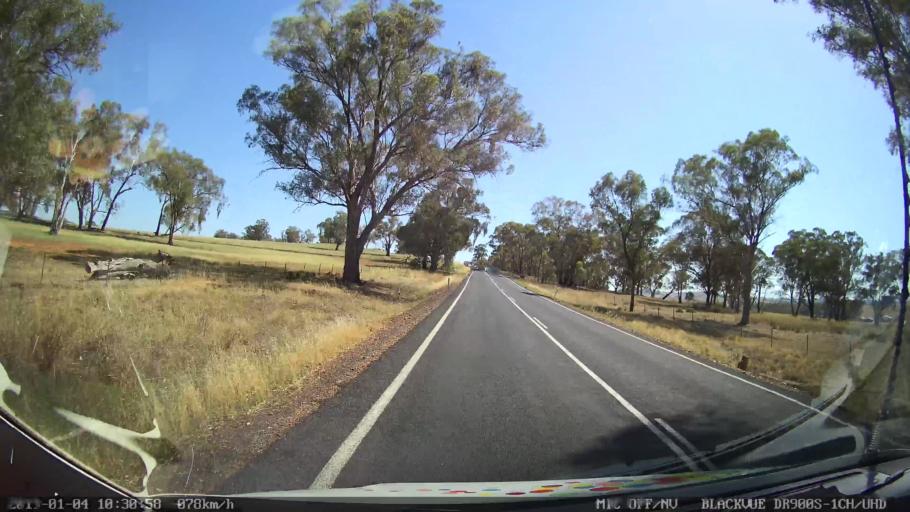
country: AU
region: New South Wales
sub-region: Cabonne
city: Canowindra
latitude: -33.3400
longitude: 148.6306
